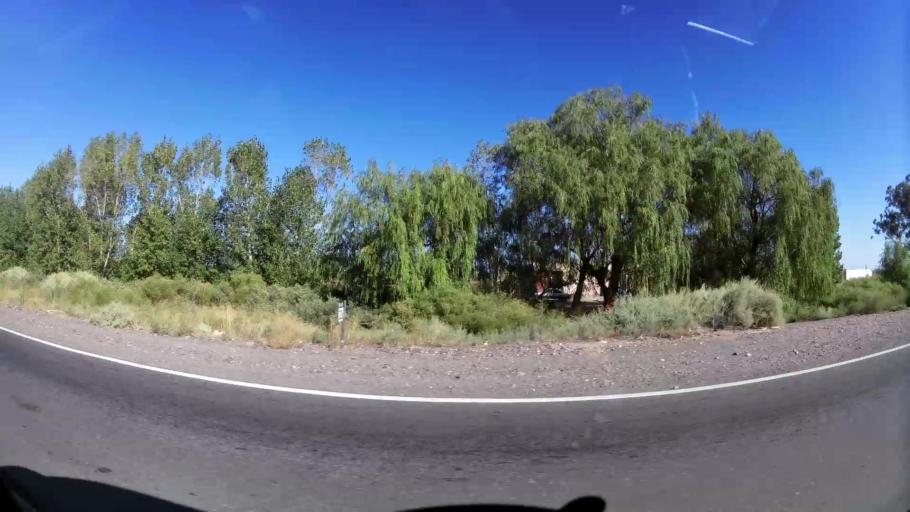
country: AR
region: Mendoza
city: General Lavalle
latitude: -32.6959
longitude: -68.6699
